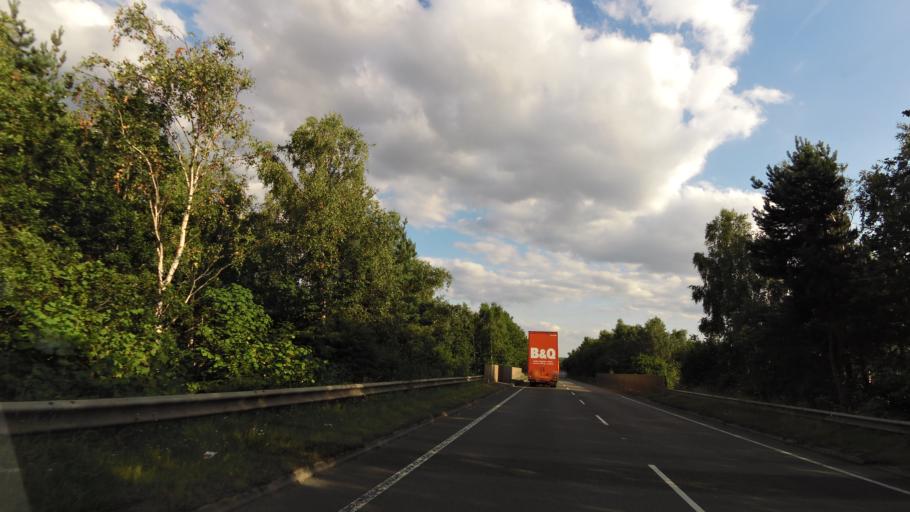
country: GB
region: England
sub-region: Nottinghamshire
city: Worksop
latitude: 53.3190
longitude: -1.1528
